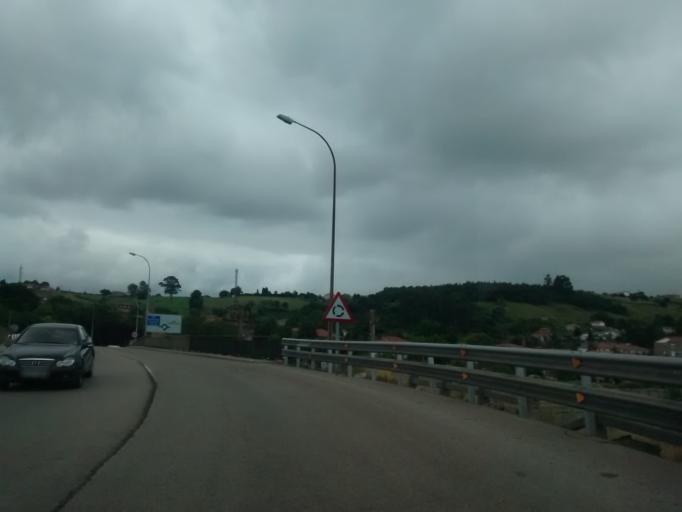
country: ES
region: Cantabria
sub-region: Provincia de Cantabria
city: Torrelavega
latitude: 43.3737
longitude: -4.0430
